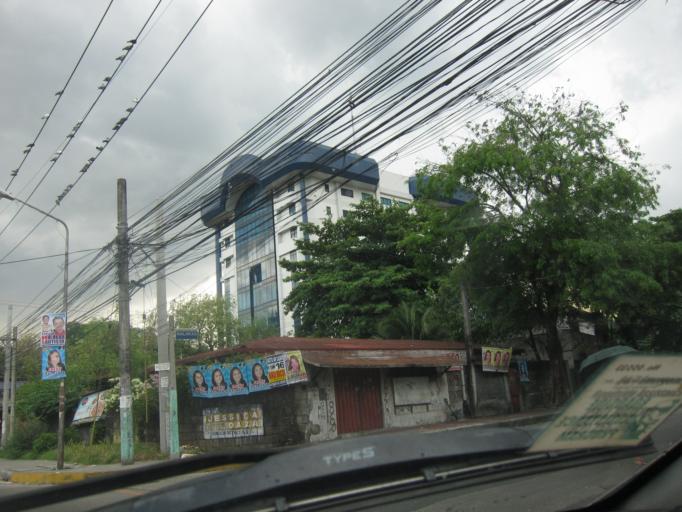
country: PH
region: Metro Manila
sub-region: Quezon City
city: Quezon City
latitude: 14.6376
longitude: 121.0482
